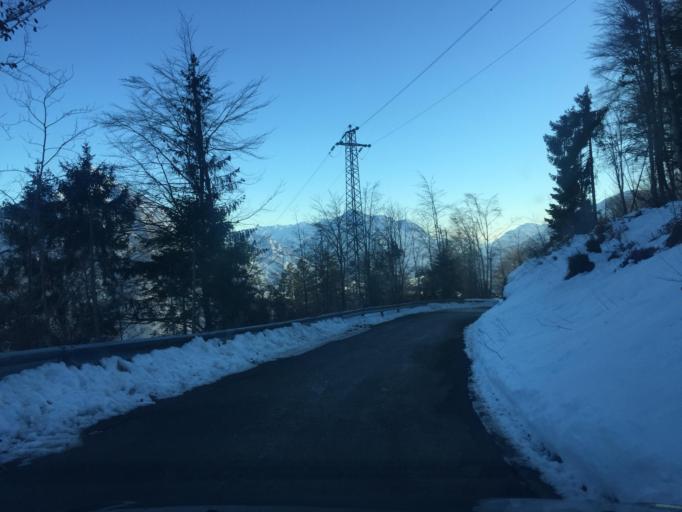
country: IT
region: Friuli Venezia Giulia
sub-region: Provincia di Udine
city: Chiaulis
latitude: 46.4248
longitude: 12.9860
